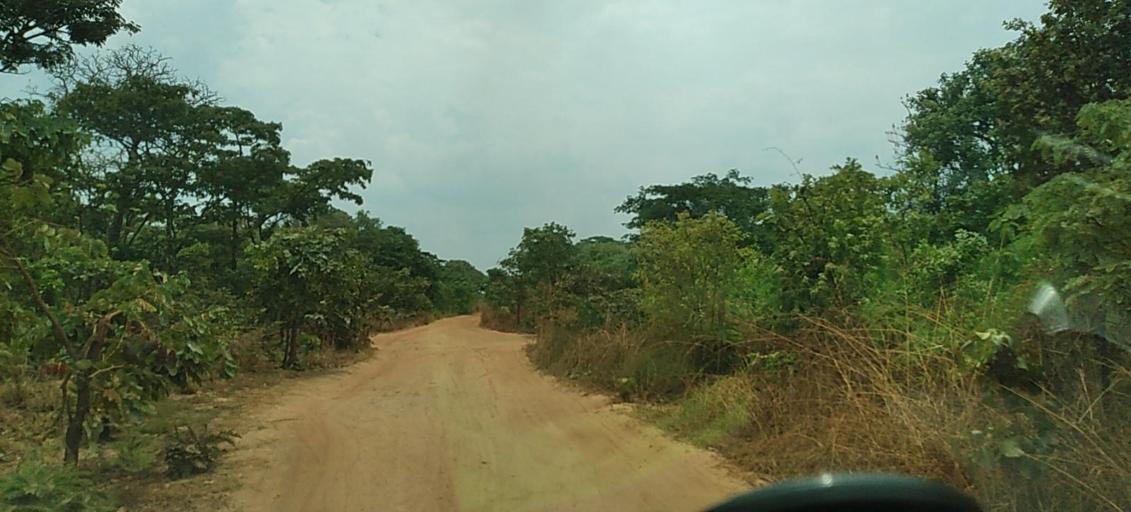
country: ZM
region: North-Western
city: Kansanshi
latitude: -12.0493
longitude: 26.3384
